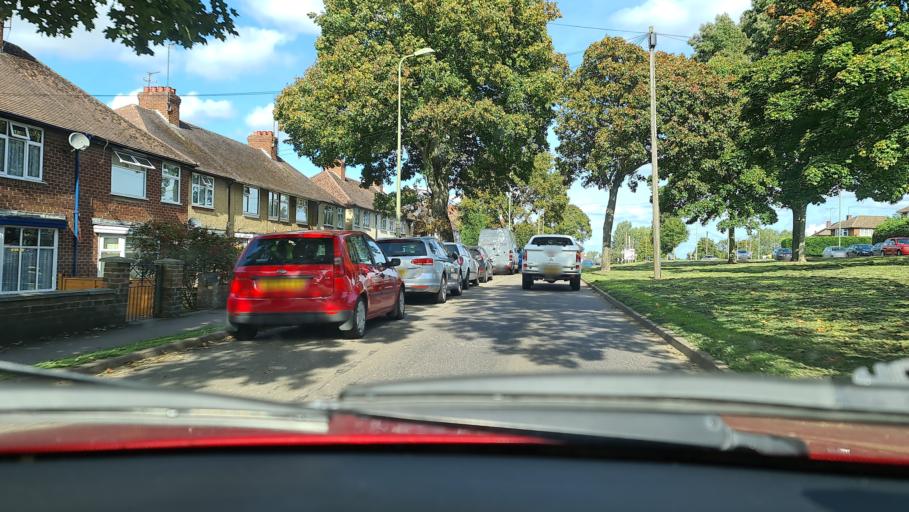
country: GB
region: England
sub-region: Oxfordshire
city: Banbury
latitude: 52.0681
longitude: -1.3501
